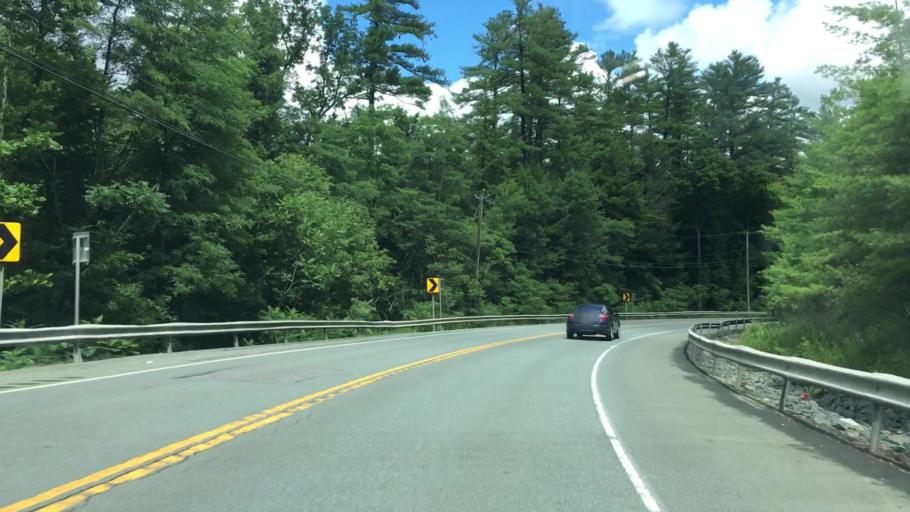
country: US
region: New York
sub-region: Rensselaer County
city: Hoosick Falls
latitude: 42.8504
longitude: -73.3504
